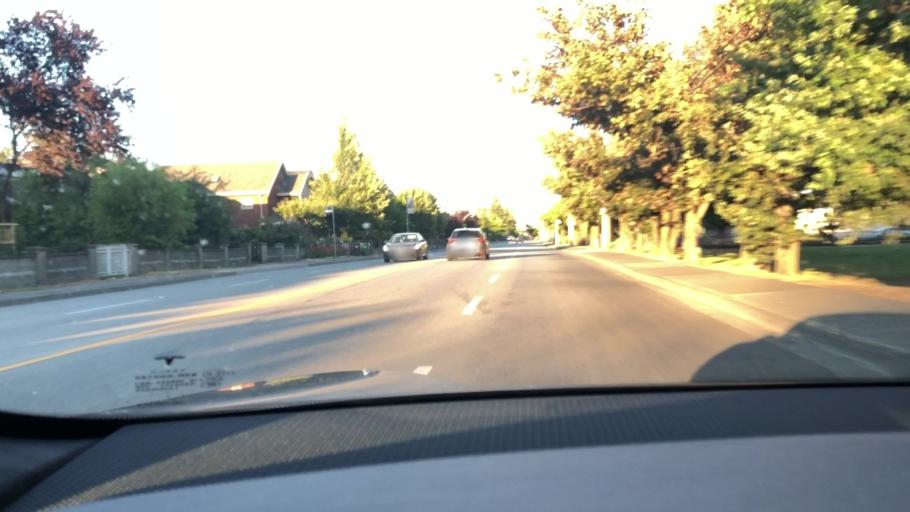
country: CA
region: British Columbia
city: Richmond
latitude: 49.1556
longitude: -123.1542
